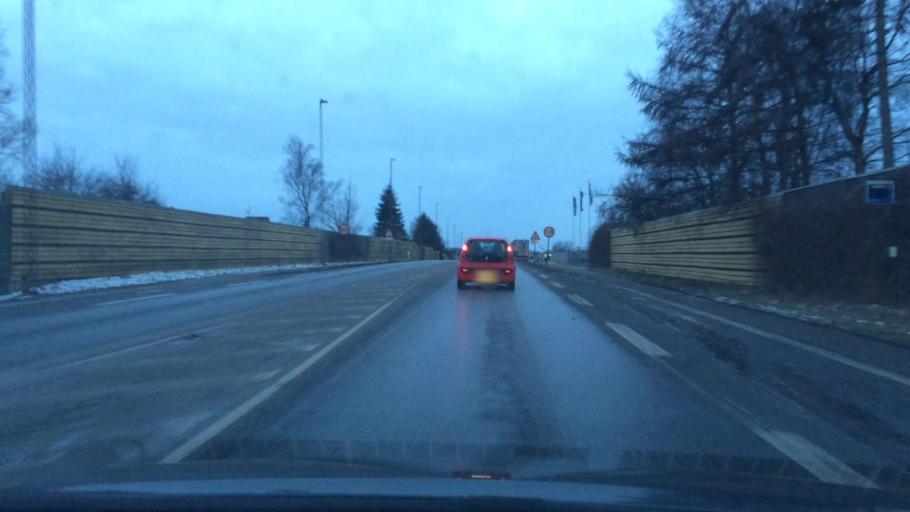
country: DK
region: Central Jutland
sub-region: Horsens Kommune
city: Horsens
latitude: 55.8360
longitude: 9.8109
